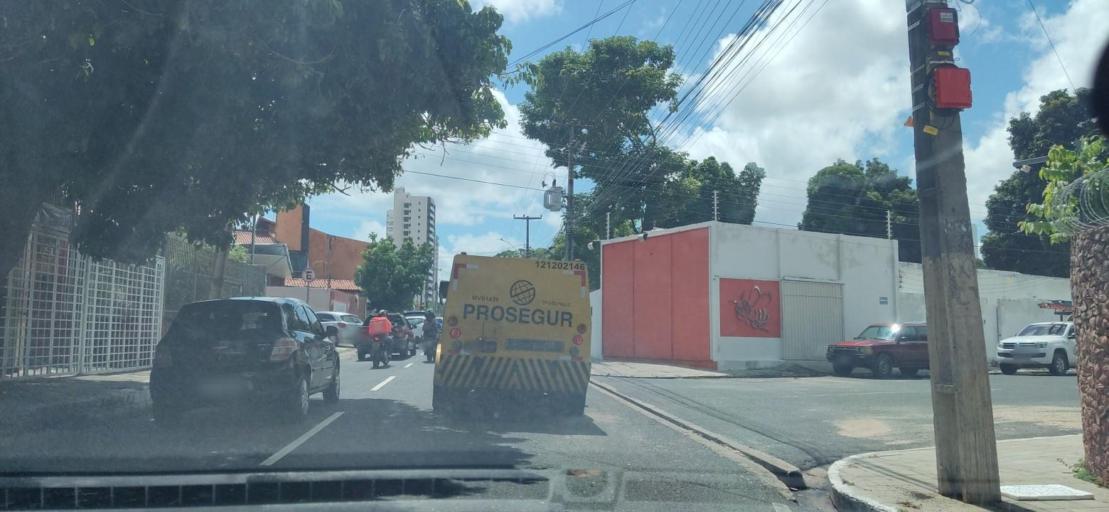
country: BR
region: Piaui
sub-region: Teresina
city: Teresina
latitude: -5.0646
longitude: -42.7855
